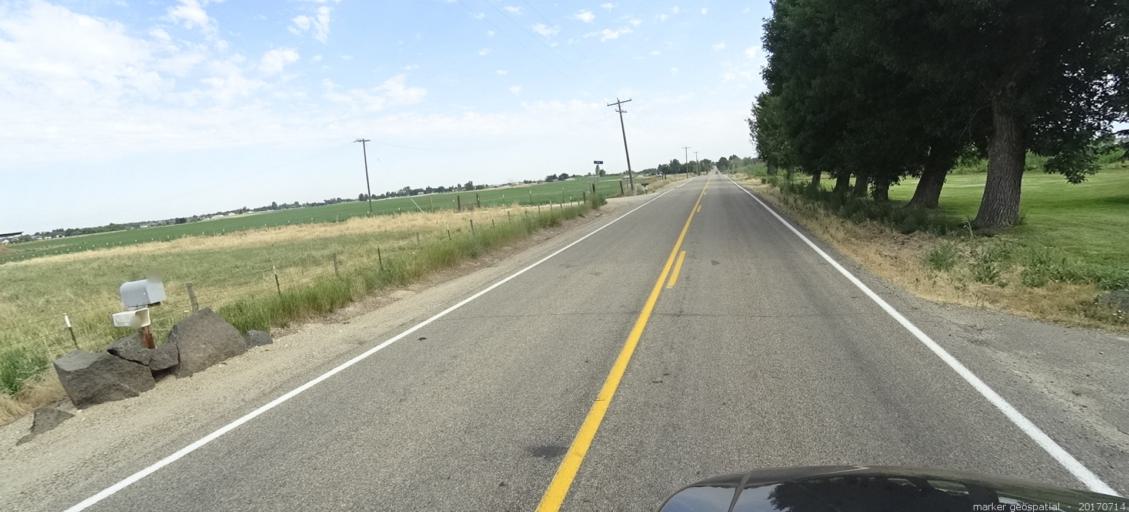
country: US
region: Idaho
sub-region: Ada County
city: Kuna
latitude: 43.4652
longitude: -116.3545
